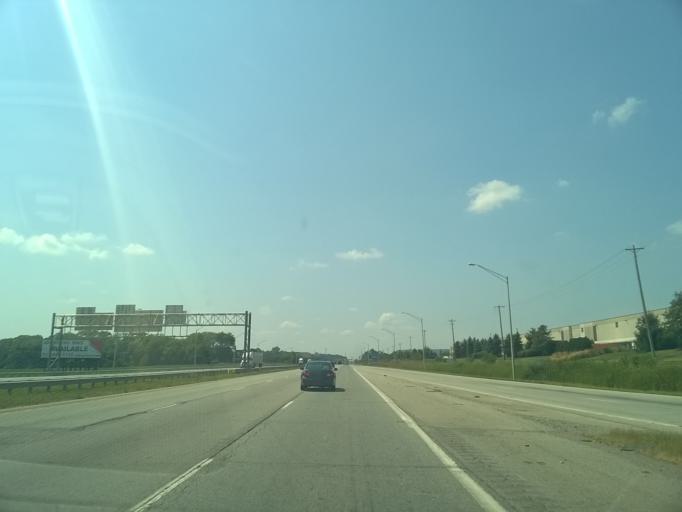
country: US
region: Indiana
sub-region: Hendricks County
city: Plainfield
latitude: 39.6786
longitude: -86.3445
